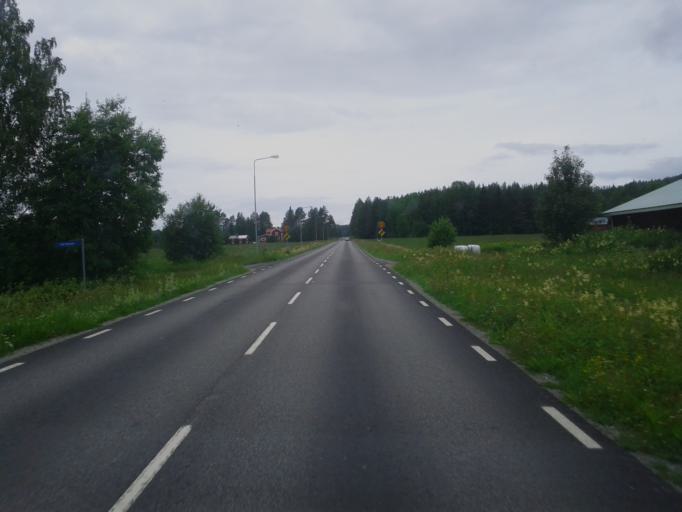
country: SE
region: Vaesterbotten
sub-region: Skelleftea Kommun
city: Viken
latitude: 64.8813
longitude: 20.7776
